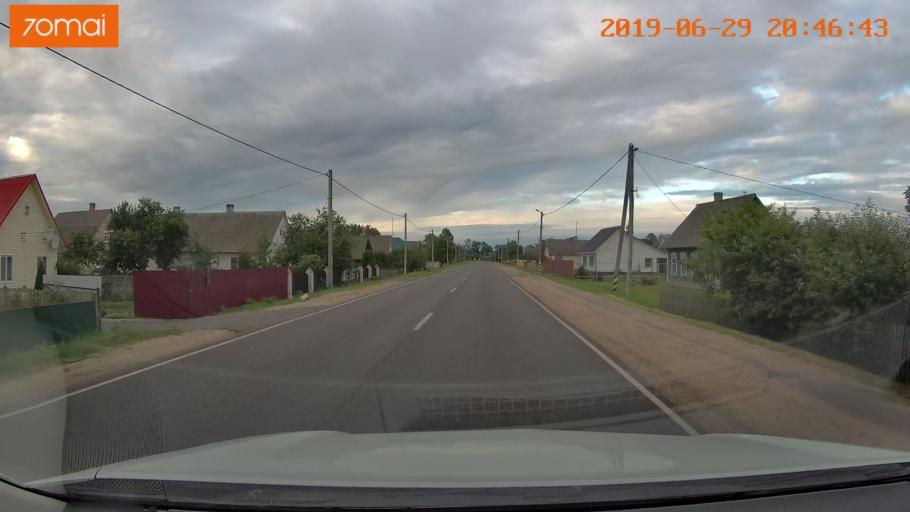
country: BY
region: Brest
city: Hantsavichy
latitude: 52.6325
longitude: 26.3104
